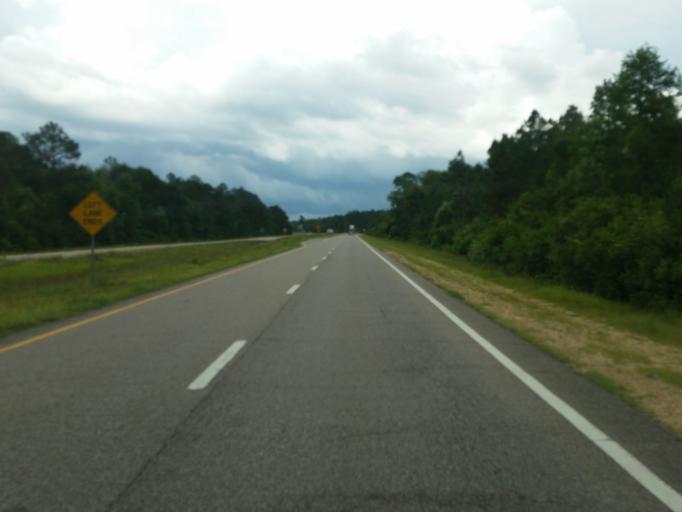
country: US
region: Mississippi
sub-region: George County
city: Lucedale
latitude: 30.8705
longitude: -88.4277
